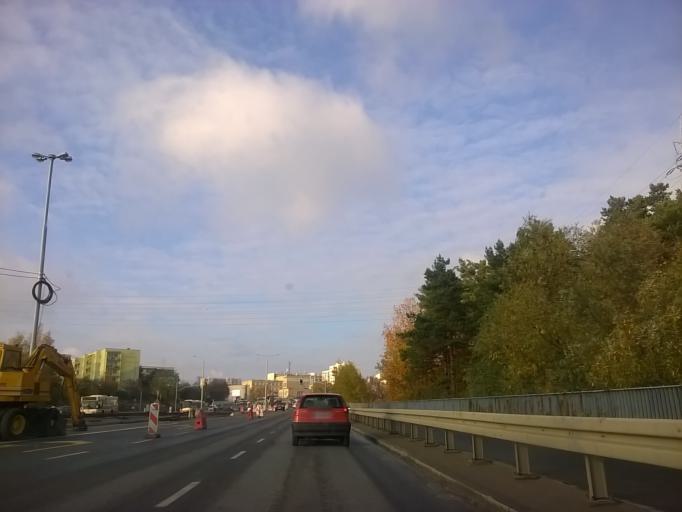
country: PL
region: Pomeranian Voivodeship
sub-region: Powiat gdanski
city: Kowale
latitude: 54.3548
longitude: 18.5894
